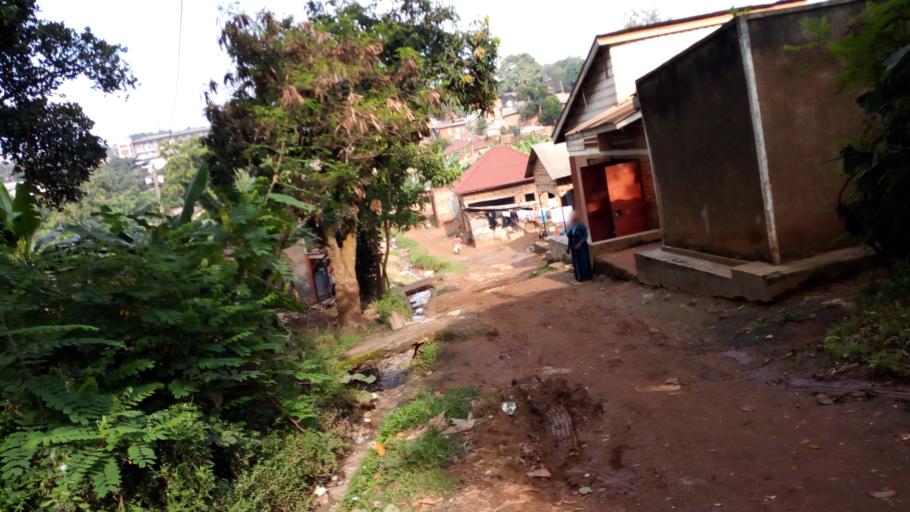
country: UG
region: Central Region
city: Kampala Central Division
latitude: 0.3708
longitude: 32.5558
